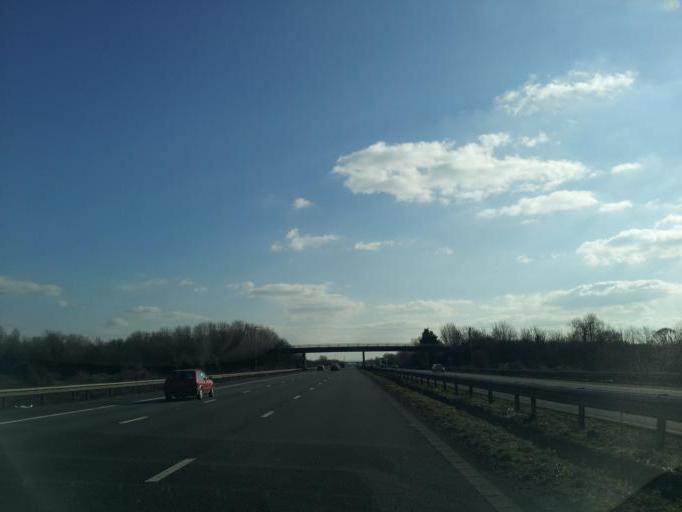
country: GB
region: England
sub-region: Somerset
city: Highbridge
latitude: 51.2086
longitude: -2.9651
